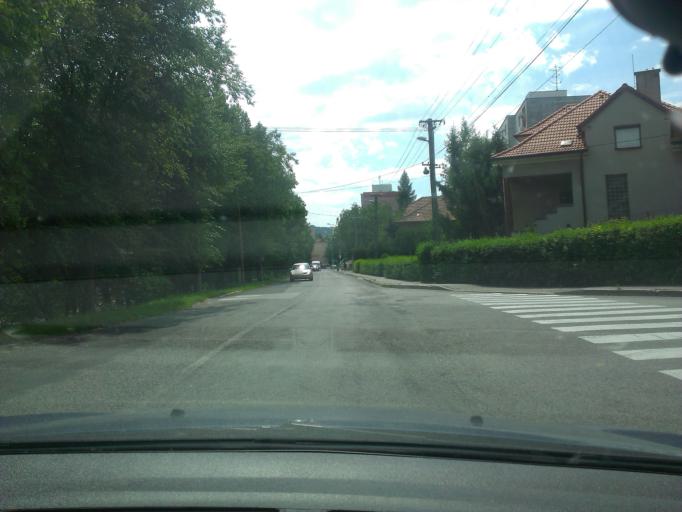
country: SK
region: Trenciansky
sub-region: Okres Myjava
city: Myjava
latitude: 48.7580
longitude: 17.5652
